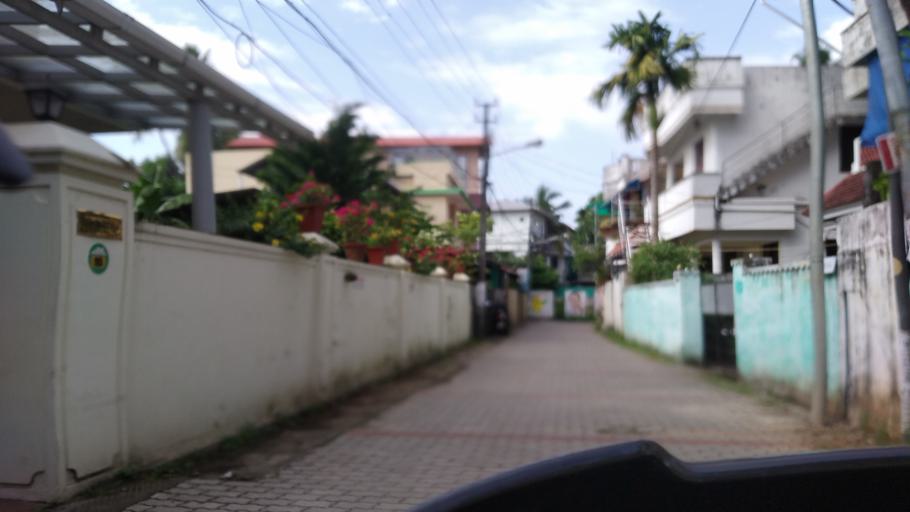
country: IN
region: Kerala
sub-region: Ernakulam
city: Cochin
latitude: 9.9870
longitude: 76.2994
